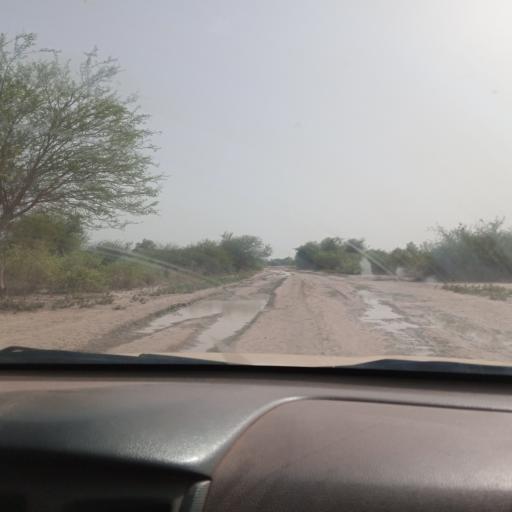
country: ML
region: Mopti
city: Tenenkou
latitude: 14.2083
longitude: -5.0119
